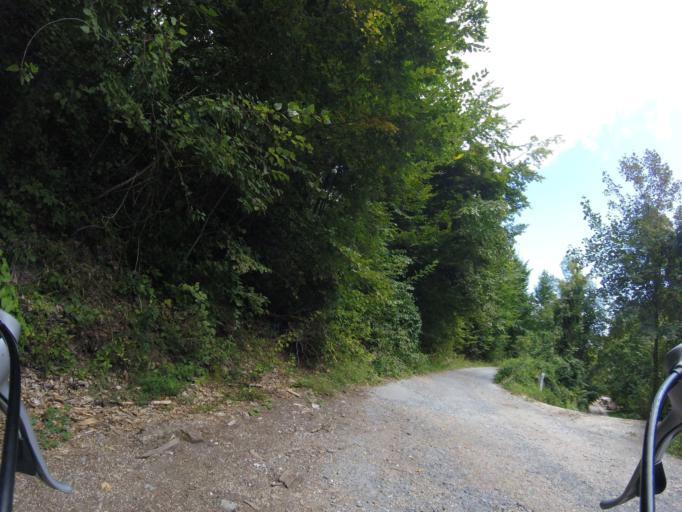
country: HU
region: Heves
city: Szilvasvarad
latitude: 48.1074
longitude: 20.5186
